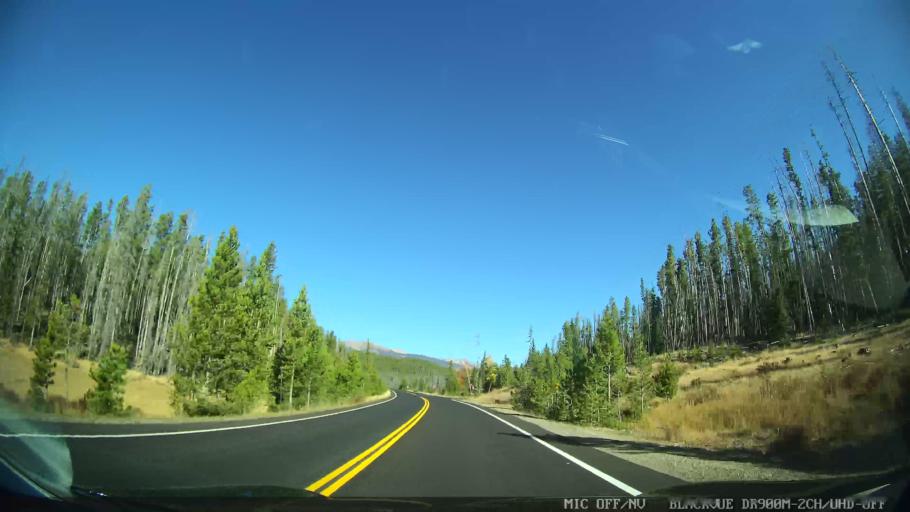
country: US
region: Colorado
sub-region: Grand County
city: Granby
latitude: 40.3143
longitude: -105.8431
